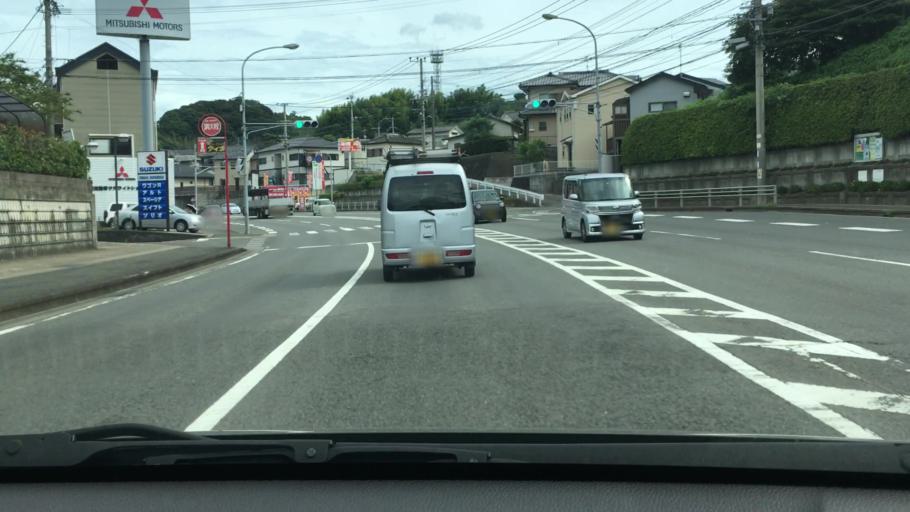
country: JP
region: Nagasaki
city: Togitsu
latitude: 32.8374
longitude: 129.8377
